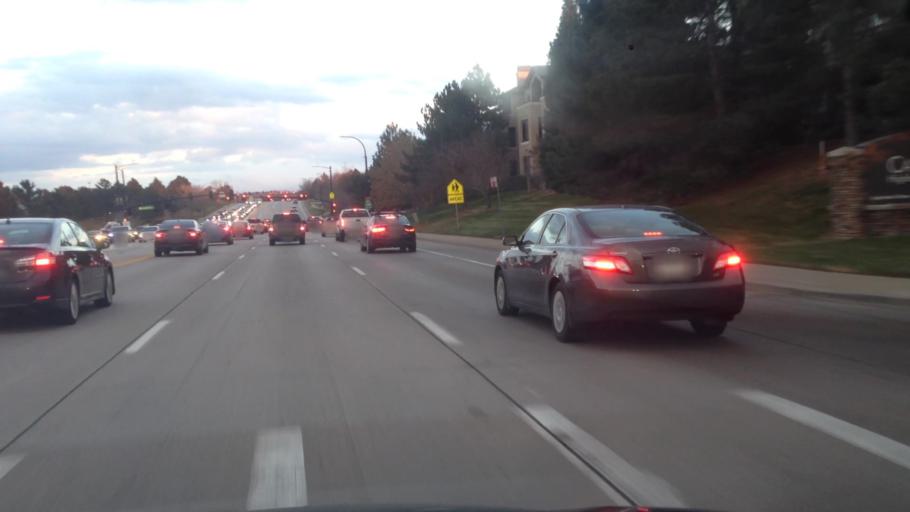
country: US
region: Colorado
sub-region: Douglas County
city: Highlands Ranch
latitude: 39.5427
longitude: -104.9376
